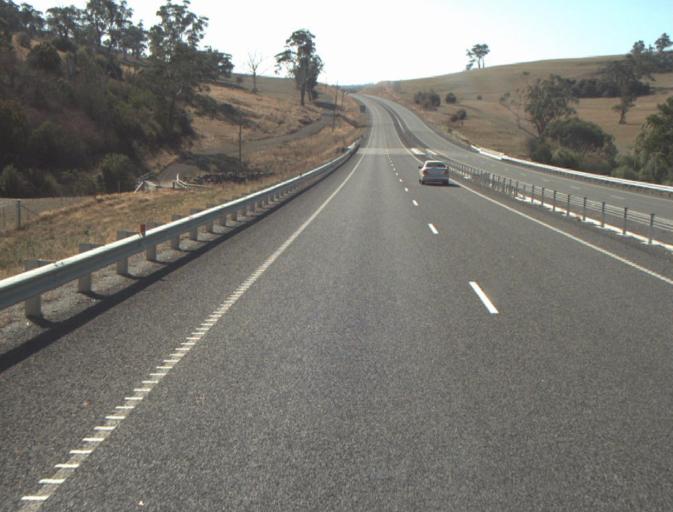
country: AU
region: Tasmania
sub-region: Launceston
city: Mayfield
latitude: -41.3631
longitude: 147.1075
